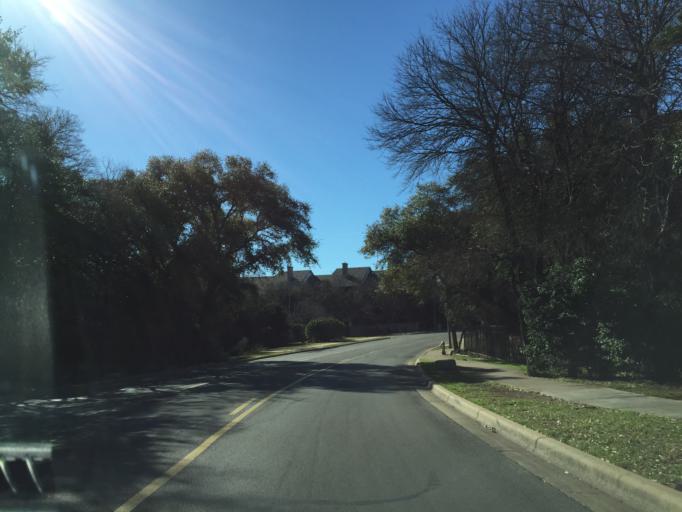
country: US
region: Texas
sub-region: Williamson County
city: Jollyville
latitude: 30.4316
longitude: -97.7440
